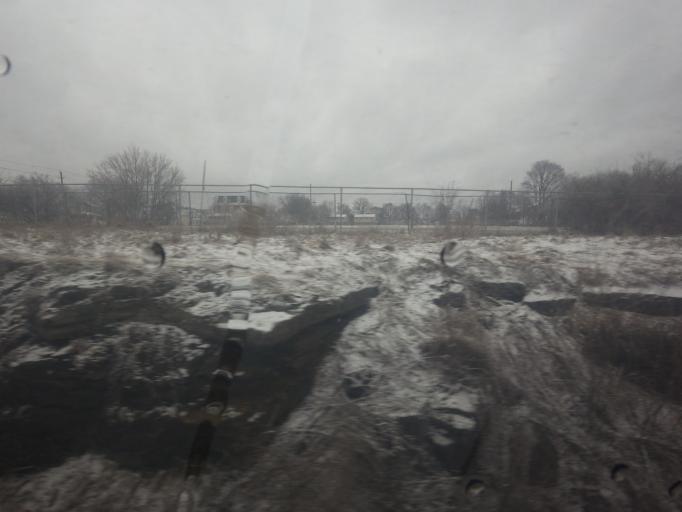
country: CA
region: Ontario
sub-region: Lanark County
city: Smiths Falls
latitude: 44.9011
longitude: -76.0121
